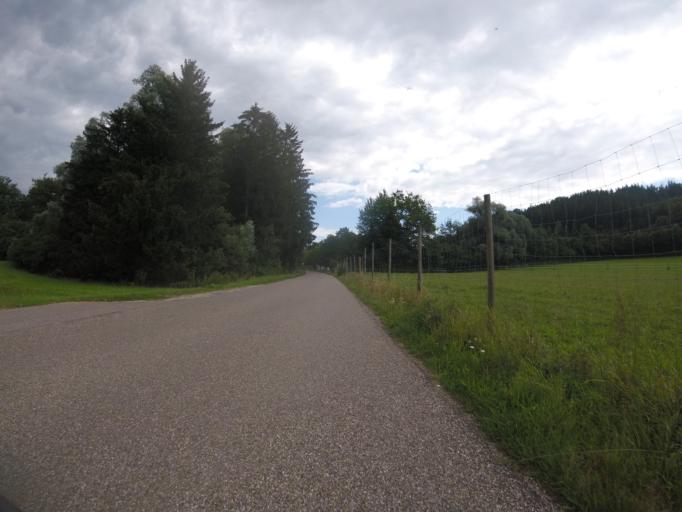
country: DE
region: Baden-Wuerttemberg
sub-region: Regierungsbezirk Stuttgart
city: Lorch
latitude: 48.7956
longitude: 9.7103
